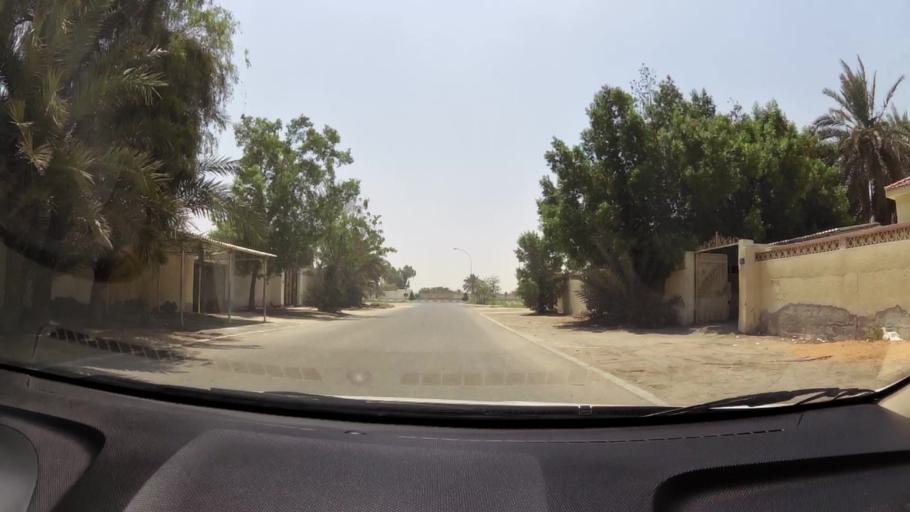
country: AE
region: Umm al Qaywayn
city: Umm al Qaywayn
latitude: 25.5585
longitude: 55.5611
